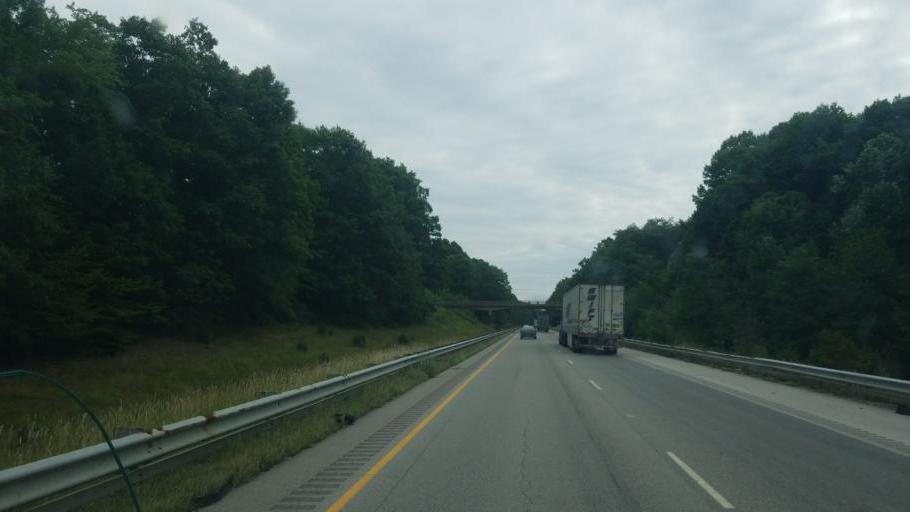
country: US
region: Indiana
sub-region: Putnam County
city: Cloverdale
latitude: 39.5171
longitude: -86.9089
